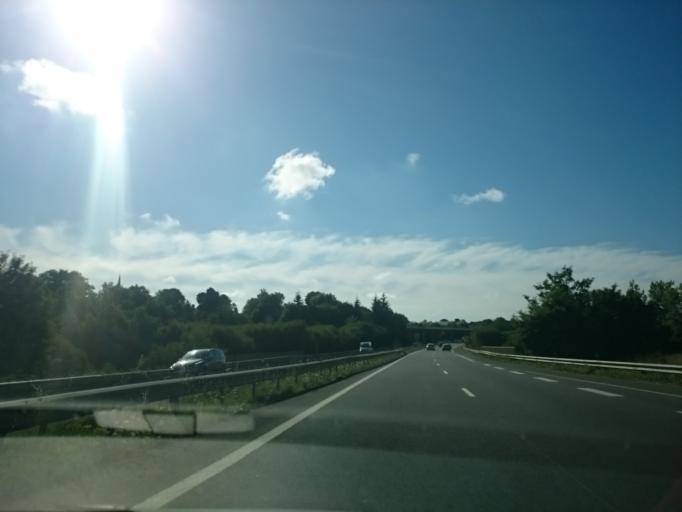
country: FR
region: Brittany
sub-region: Departement d'Ille-et-Vilaine
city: Quedillac
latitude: 48.2670
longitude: -2.1496
